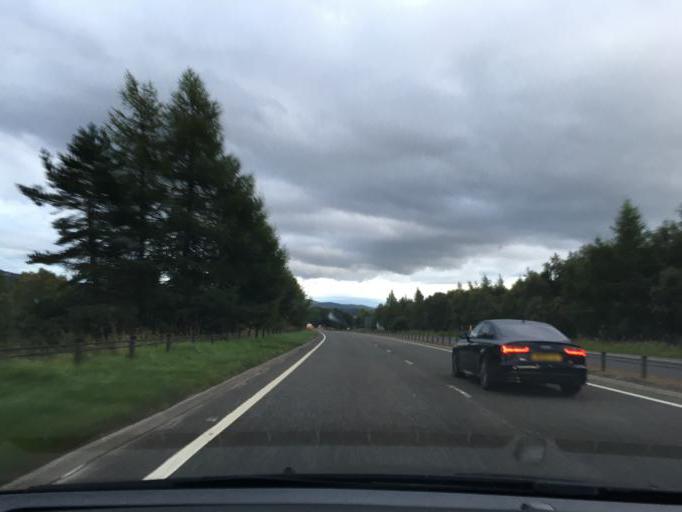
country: GB
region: Scotland
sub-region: Highland
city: Inverness
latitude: 57.4355
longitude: -4.1362
